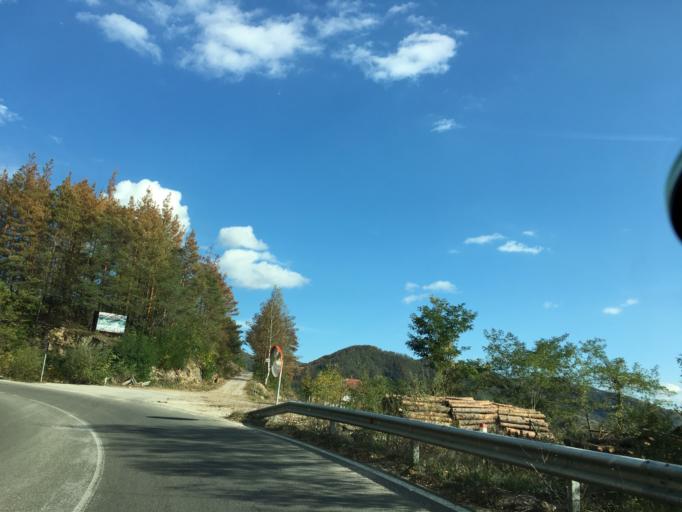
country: BG
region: Smolyan
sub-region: Obshtina Madan
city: Madan
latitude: 41.5346
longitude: 24.9179
